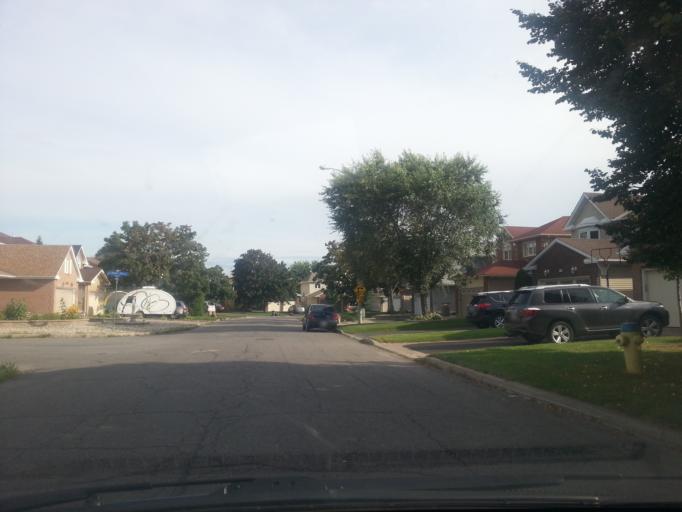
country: CA
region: Quebec
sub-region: Outaouais
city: Gatineau
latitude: 45.4562
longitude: -75.5281
